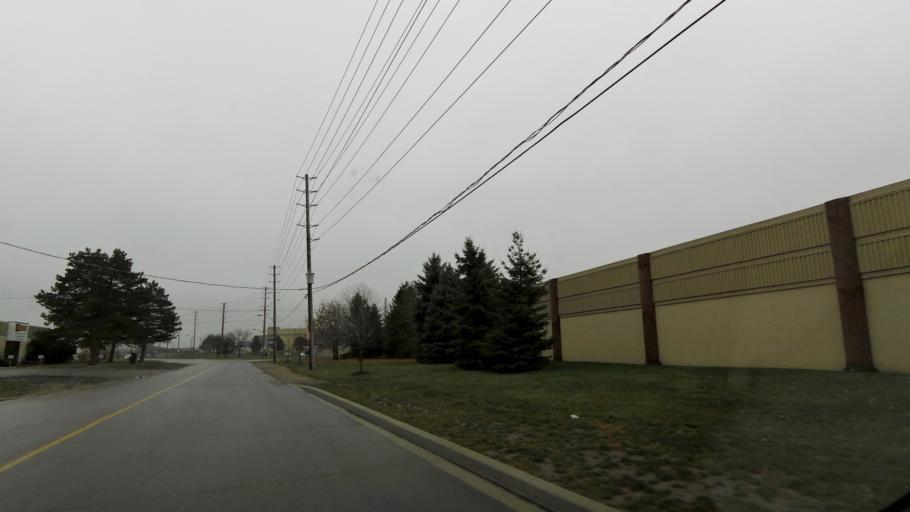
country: CA
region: Ontario
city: Etobicoke
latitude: 43.7043
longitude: -79.6034
